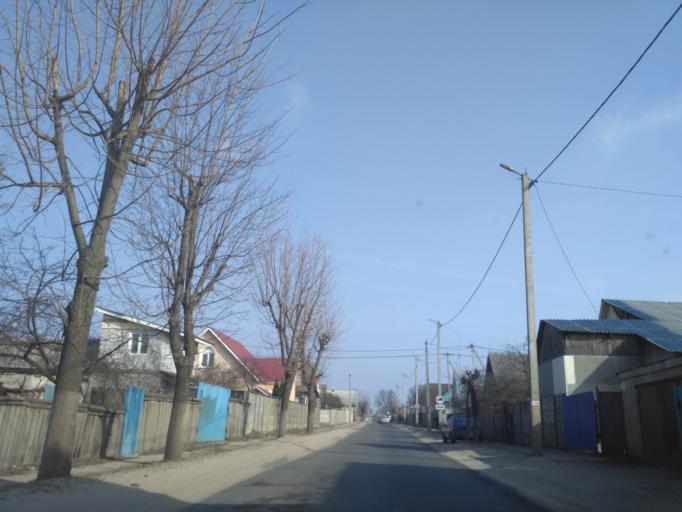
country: BY
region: Minsk
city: Horad Barysaw
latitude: 54.2478
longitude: 28.5064
